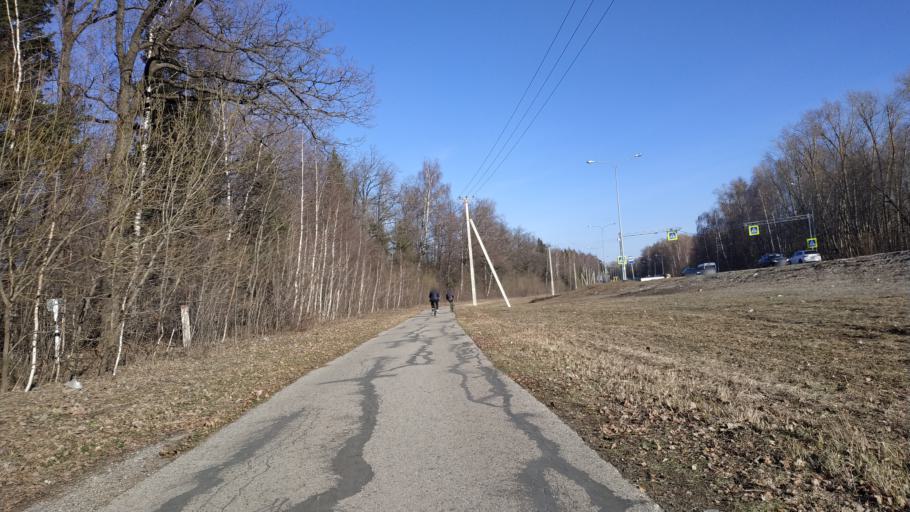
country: RU
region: Chuvashia
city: Novyye Lapsary
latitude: 56.1328
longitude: 47.1090
